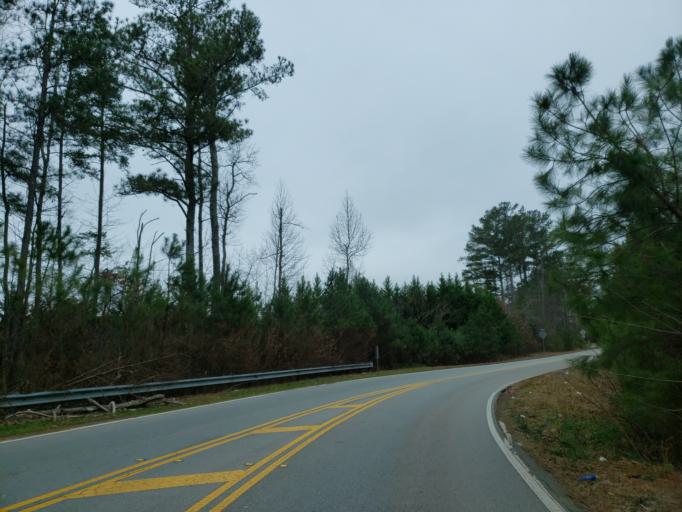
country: US
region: Georgia
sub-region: Paulding County
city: Hiram
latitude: 33.9374
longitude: -84.7120
